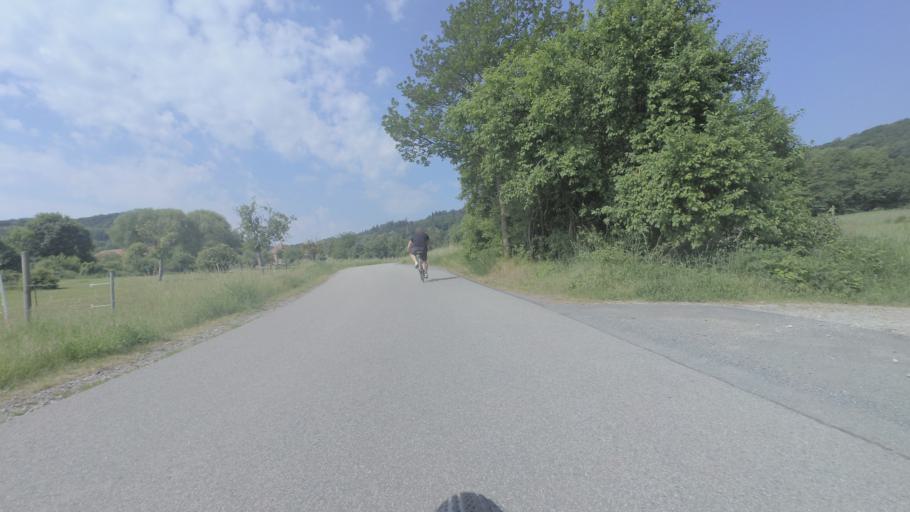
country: DE
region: Saxony-Anhalt
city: Huttenrode
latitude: 51.8081
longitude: 10.9166
